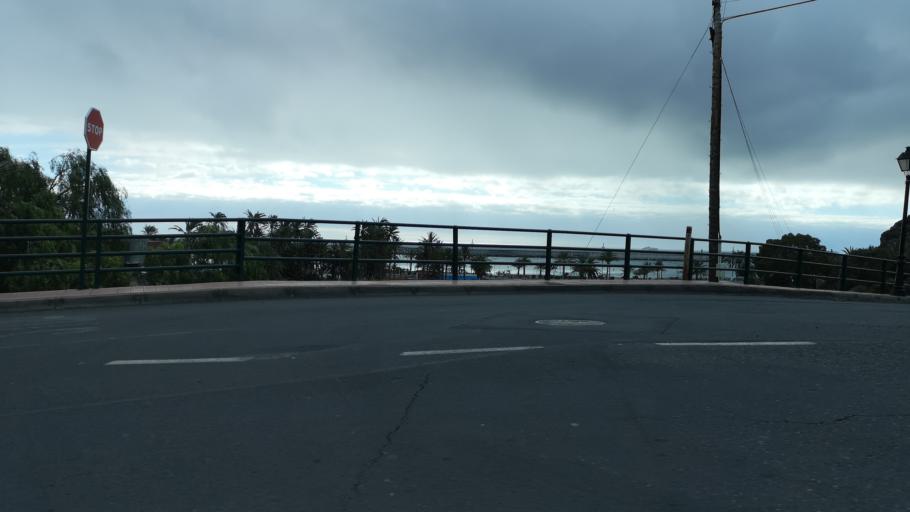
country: ES
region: Canary Islands
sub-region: Provincia de Santa Cruz de Tenerife
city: San Sebastian de la Gomera
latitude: 28.0897
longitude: -17.1148
